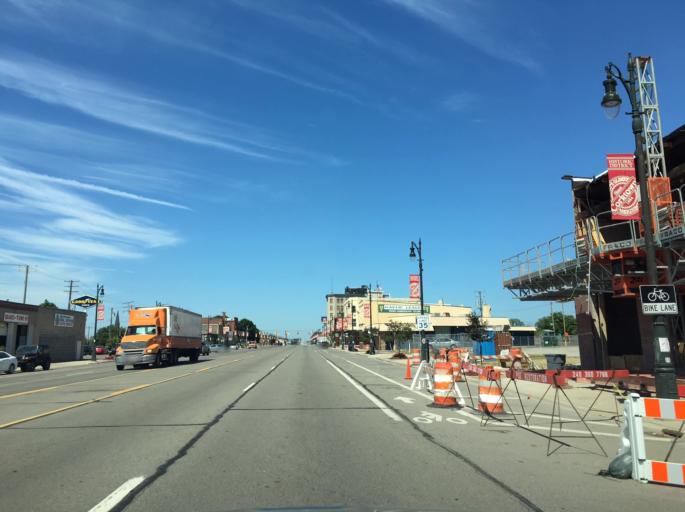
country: US
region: Michigan
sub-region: Wayne County
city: Detroit
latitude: 42.3315
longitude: -83.0734
